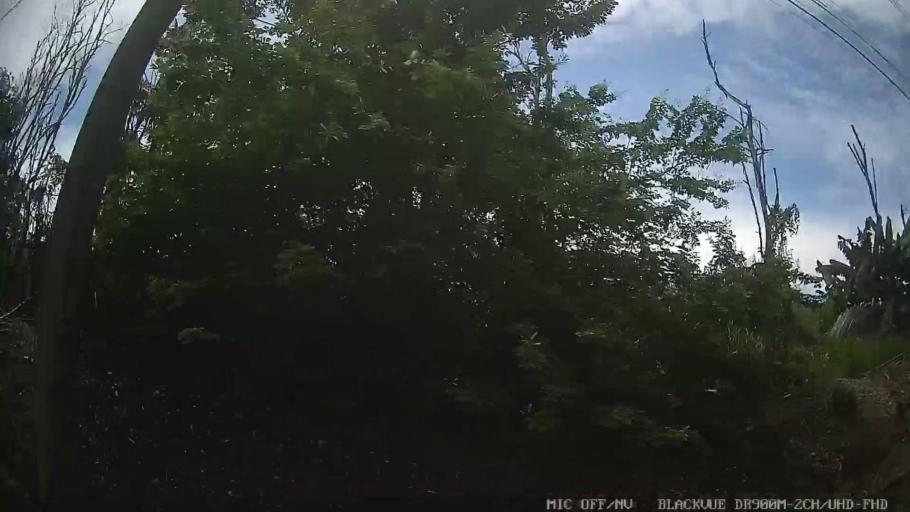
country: BR
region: Sao Paulo
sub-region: Santa Isabel
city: Santa Isabel
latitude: -23.4008
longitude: -46.1976
